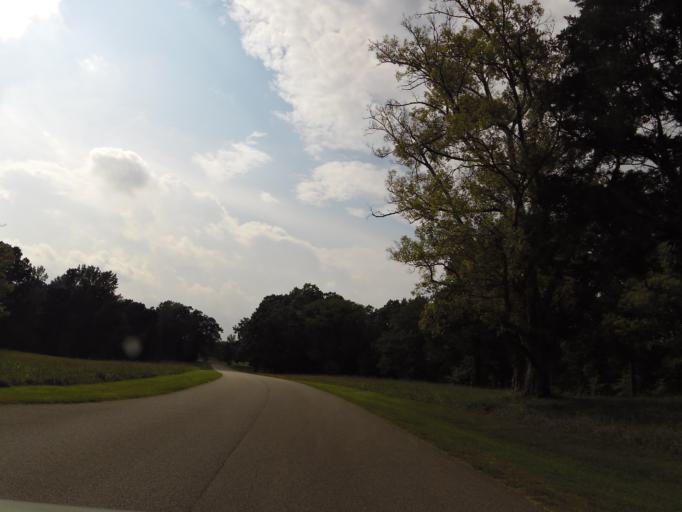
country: US
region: Tennessee
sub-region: Hardin County
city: Crump
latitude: 35.1527
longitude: -88.3327
